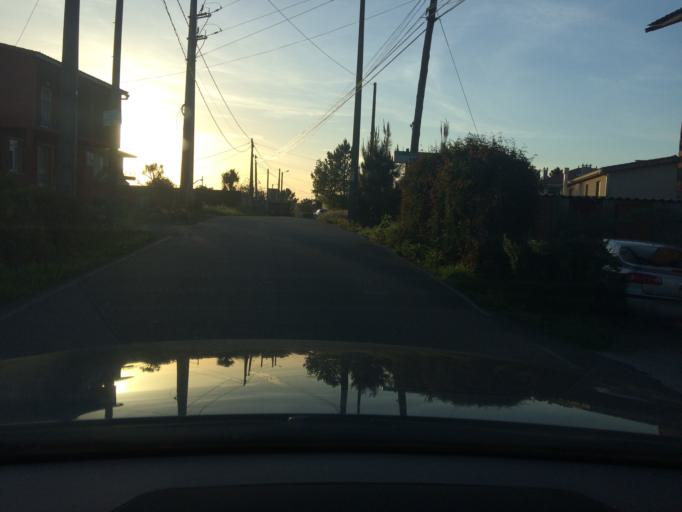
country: ES
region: Galicia
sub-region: Provincia da Coruna
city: Santiago de Compostela
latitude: 42.8338
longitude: -8.6017
